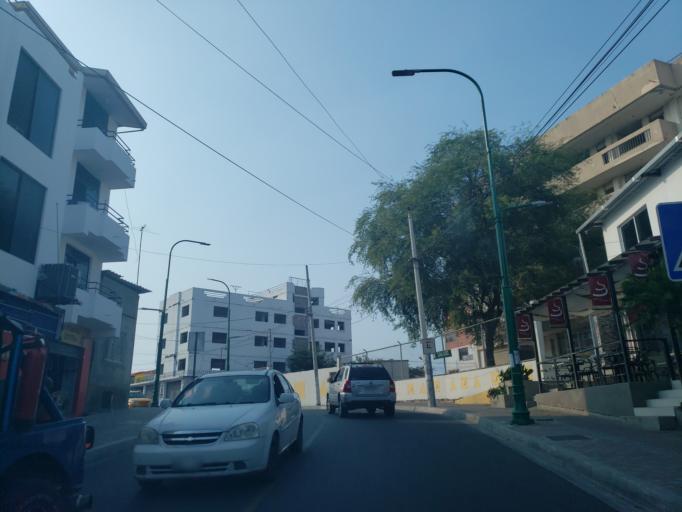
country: EC
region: Manabi
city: Manta
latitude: -0.9456
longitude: -80.7281
